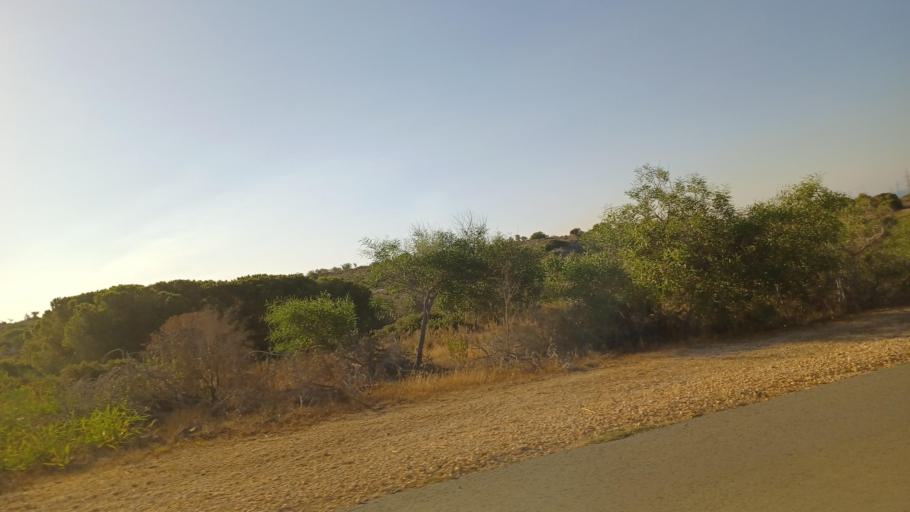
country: CY
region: Larnaka
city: Xylotymbou
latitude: 34.9935
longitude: 33.7424
